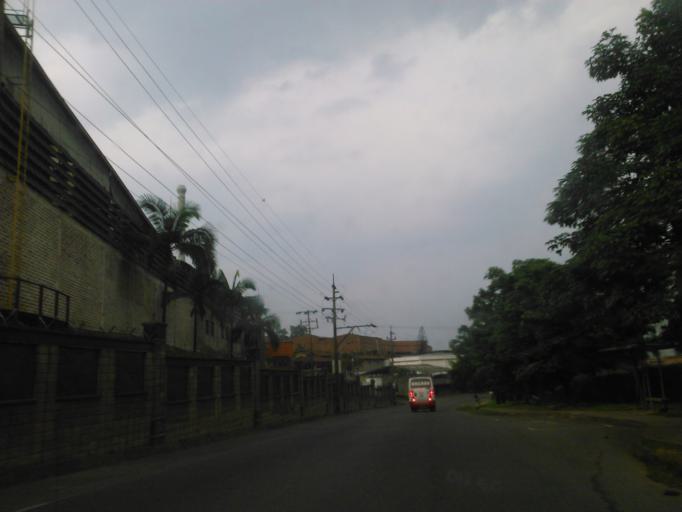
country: CO
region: Antioquia
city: La Estrella
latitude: 6.1512
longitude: -75.6355
